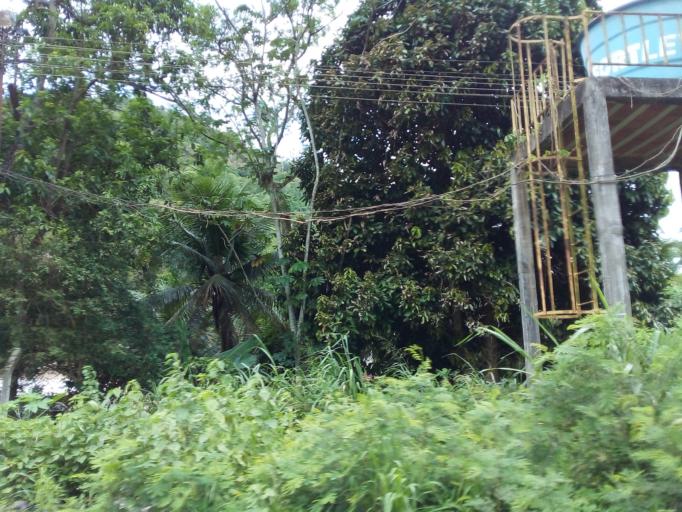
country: BR
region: Espirito Santo
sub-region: Joao Neiva
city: Joao Neiva
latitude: -19.7488
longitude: -40.3662
